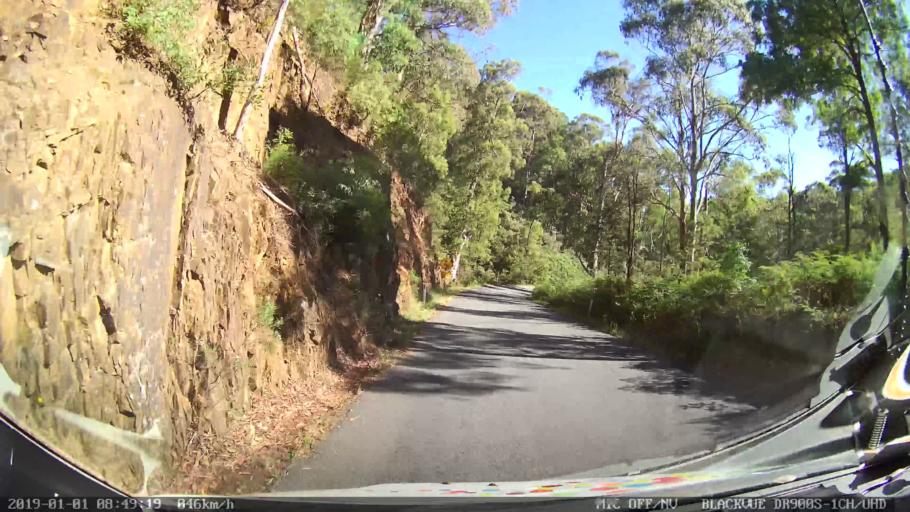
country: AU
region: New South Wales
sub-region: Snowy River
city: Jindabyne
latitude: -36.2832
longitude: 148.1995
